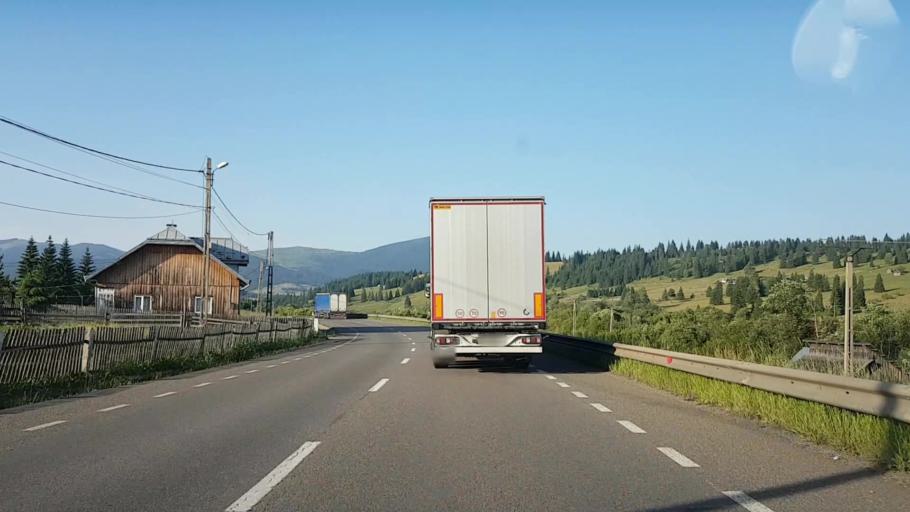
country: RO
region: Suceava
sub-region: Comuna Cosna
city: Cosna
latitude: 47.3395
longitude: 25.1734
